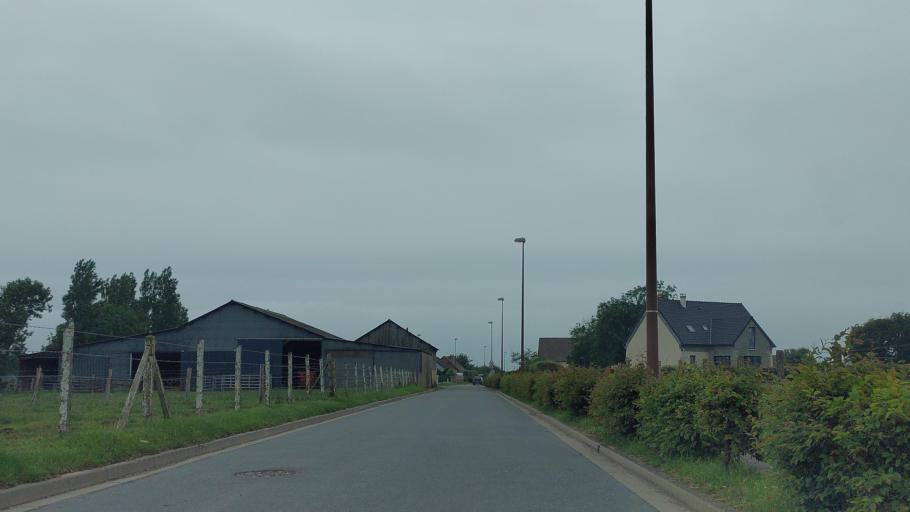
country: FR
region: Picardie
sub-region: Departement de la Somme
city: Ault
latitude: 50.0988
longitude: 1.4593
